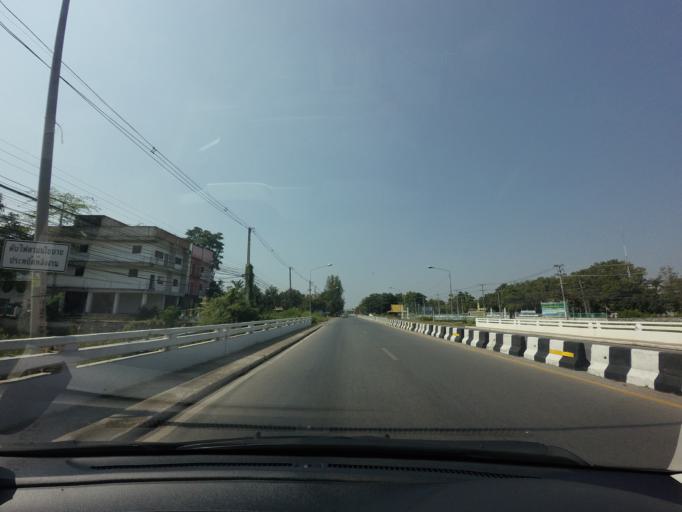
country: TH
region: Sukhothai
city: Sukhothai
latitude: 17.0100
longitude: 99.7950
